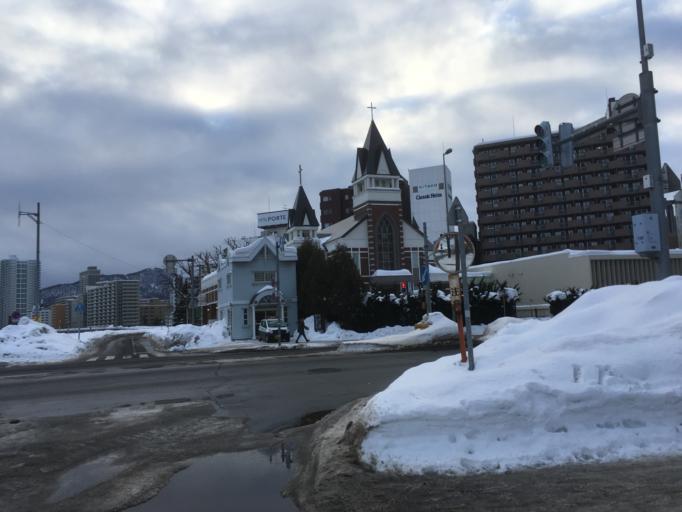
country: JP
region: Hokkaido
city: Sapporo
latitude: 43.0563
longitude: 141.3639
